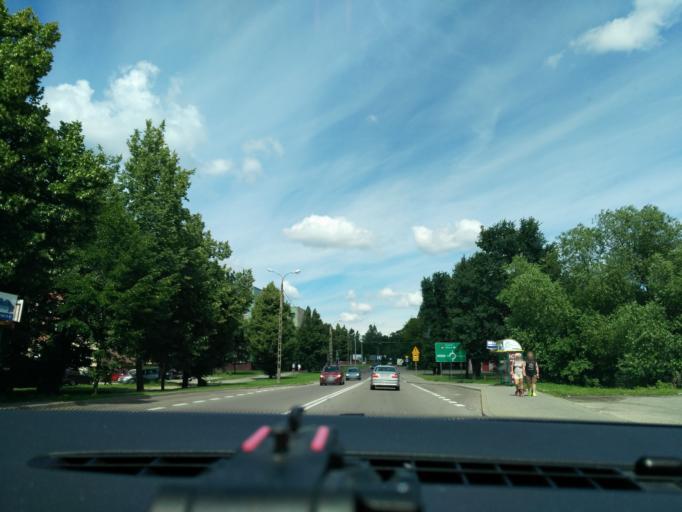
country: PL
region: Podlasie
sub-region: Powiat augustowski
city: Augustow
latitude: 53.8384
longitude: 22.9888
